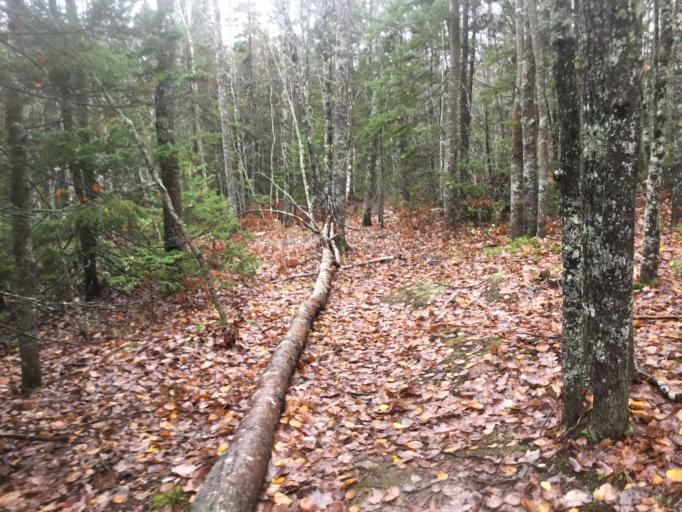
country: CA
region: Nova Scotia
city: New Glasgow
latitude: 45.5500
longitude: -62.6817
